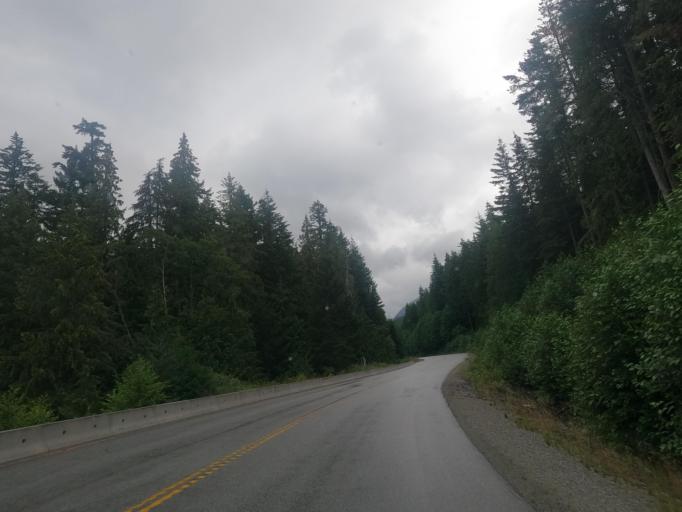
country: CA
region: British Columbia
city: Pemberton
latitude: 50.3220
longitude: -122.5609
